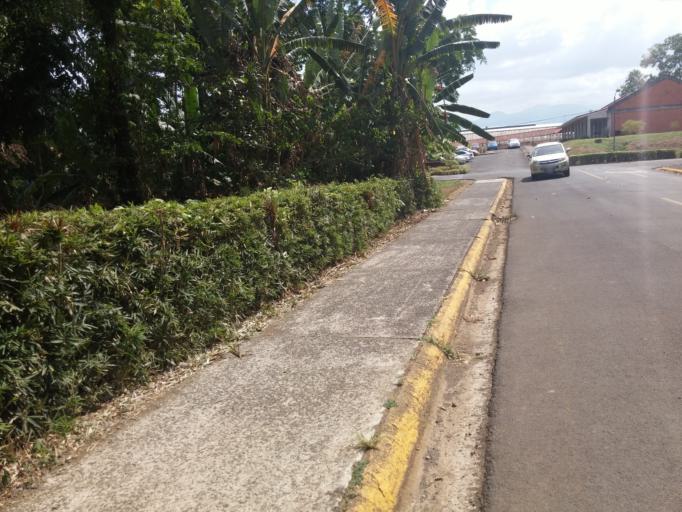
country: CR
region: Alajuela
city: Quesada
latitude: 10.3630
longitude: -84.5096
